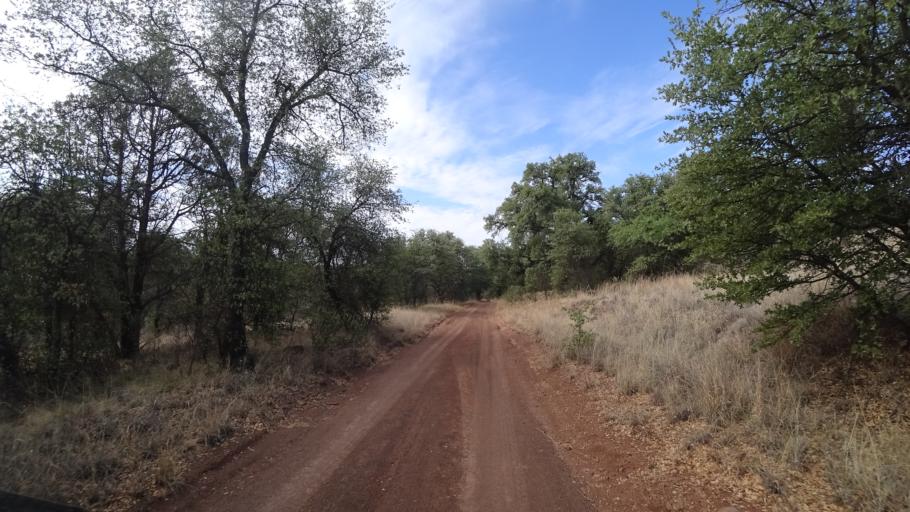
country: MX
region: Sonora
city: Santa Cruz
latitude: 31.4853
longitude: -110.5709
